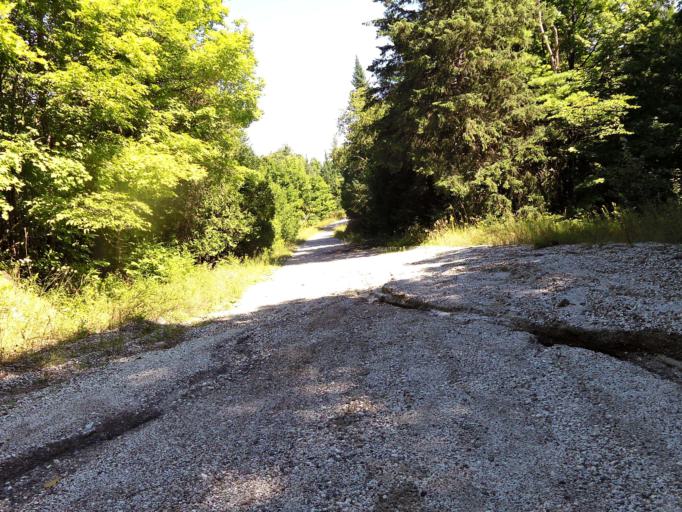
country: CA
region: Ontario
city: Arnprior
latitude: 45.1614
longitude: -76.4911
